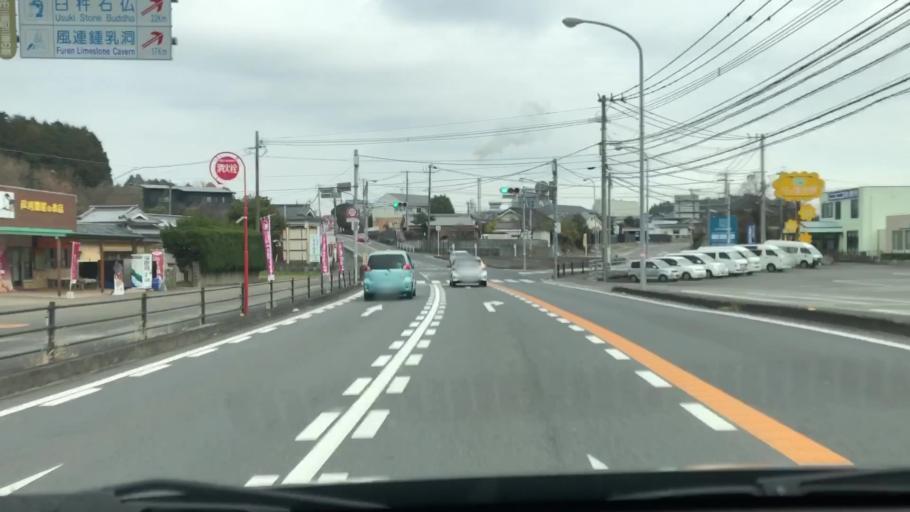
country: JP
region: Oita
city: Takedamachi
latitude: 32.9962
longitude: 131.6162
